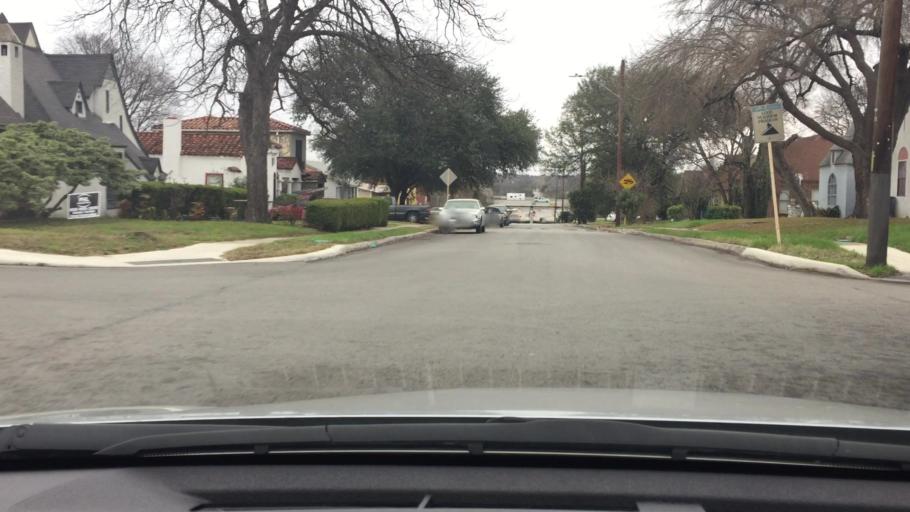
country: US
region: Texas
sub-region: Bexar County
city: Olmos Park
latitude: 29.4616
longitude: -98.5189
